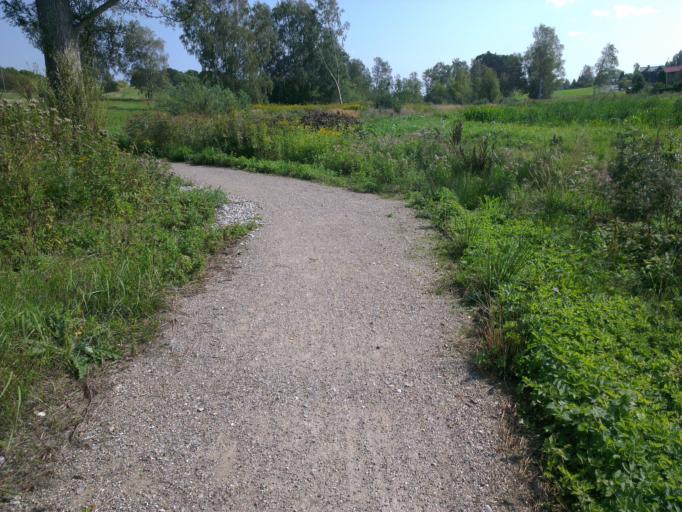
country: DK
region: Capital Region
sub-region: Frederikssund Kommune
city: Frederikssund
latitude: 55.8372
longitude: 12.0756
